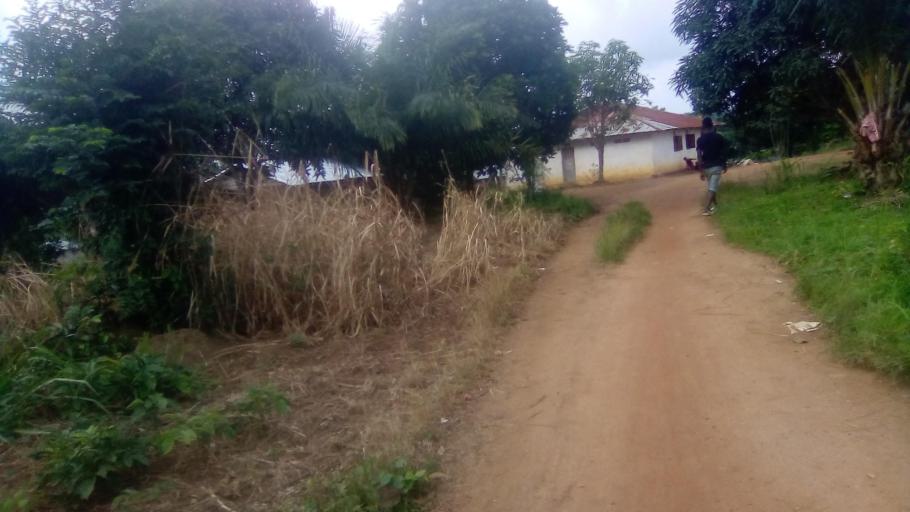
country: SL
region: Eastern Province
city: Kailahun
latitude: 8.2729
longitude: -10.5681
